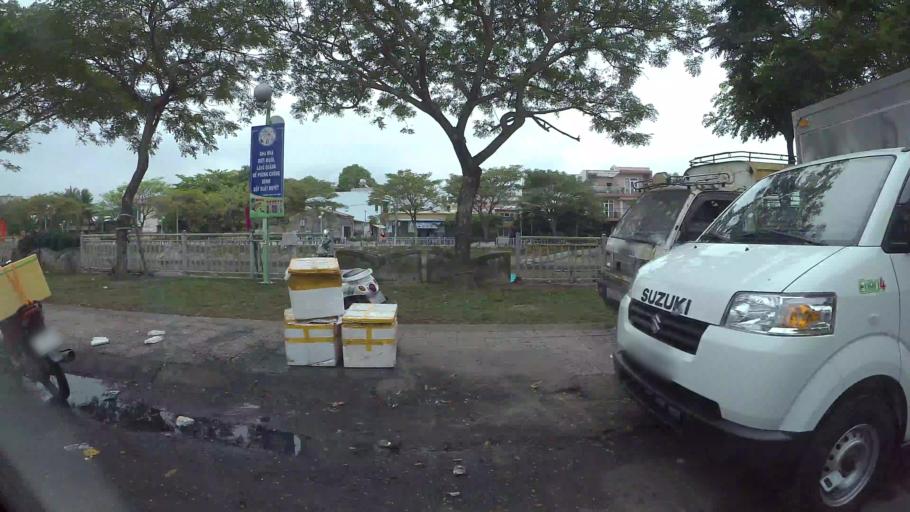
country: VN
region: Da Nang
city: Thanh Khe
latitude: 16.0730
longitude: 108.1805
